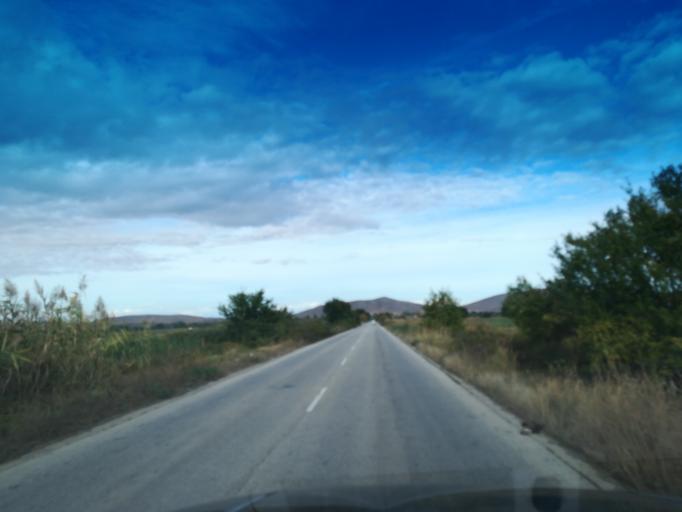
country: BG
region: Plovdiv
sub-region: Obshtina Krichim
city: Krichim
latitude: 42.0734
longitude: 24.4078
